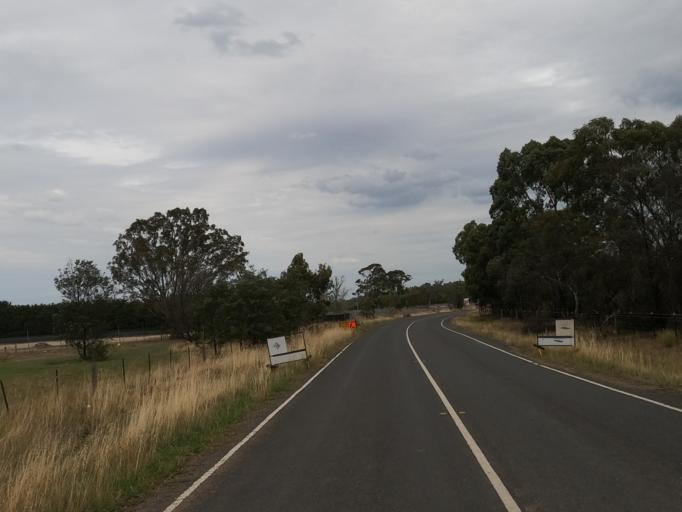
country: AU
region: Victoria
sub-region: Hume
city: Greenvale
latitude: -37.6391
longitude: 144.8714
